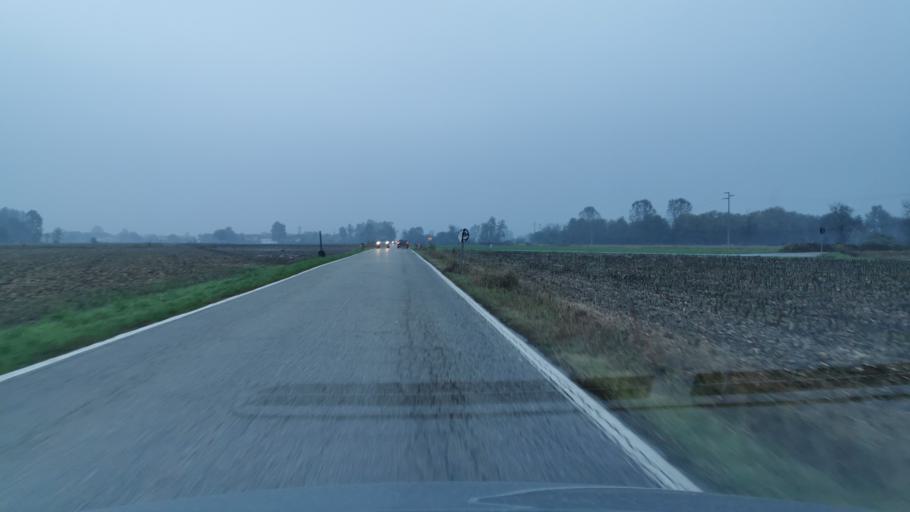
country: IT
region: Piedmont
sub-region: Provincia di Torino
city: Lusiglie
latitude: 45.3197
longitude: 7.7596
